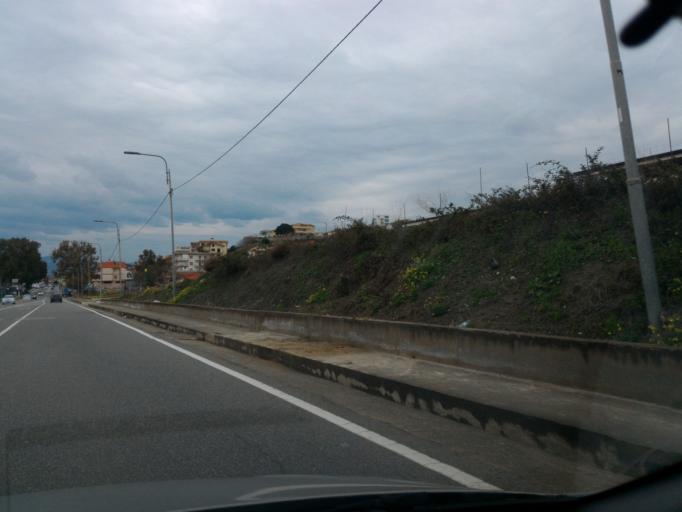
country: IT
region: Calabria
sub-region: Provincia di Catanzaro
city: Barone
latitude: 38.8355
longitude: 16.6363
